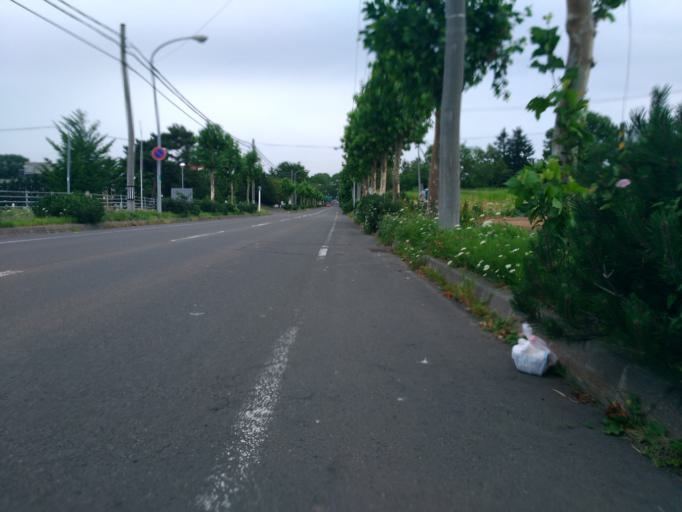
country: JP
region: Hokkaido
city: Ebetsu
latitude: 43.0678
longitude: 141.5022
